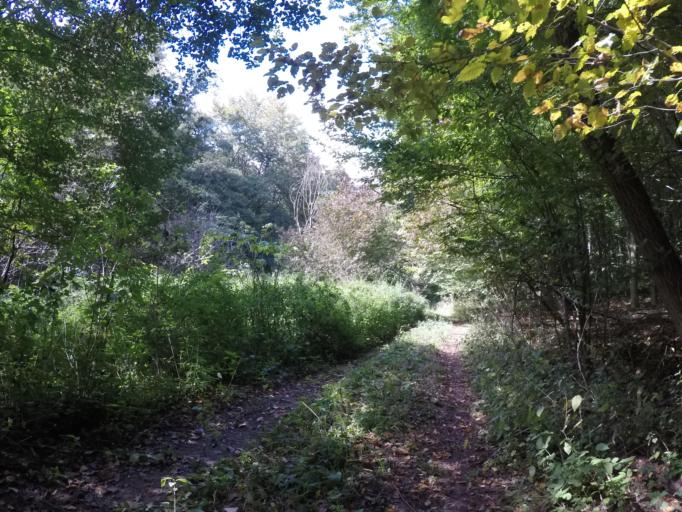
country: SK
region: Presovsky
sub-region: Okres Presov
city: Presov
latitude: 48.9373
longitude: 21.1492
